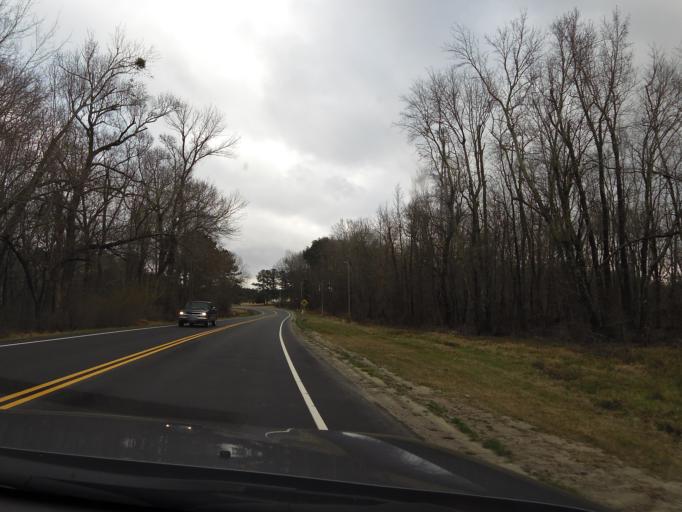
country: US
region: North Carolina
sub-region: Nash County
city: Rocky Mount
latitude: 35.8708
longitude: -77.7374
